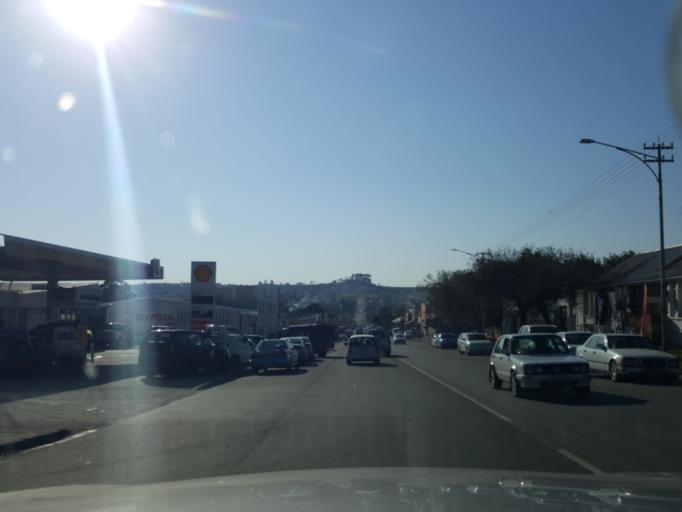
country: ZA
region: Eastern Cape
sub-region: Cacadu District Municipality
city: Grahamstown
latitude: -33.3129
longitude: 26.5296
